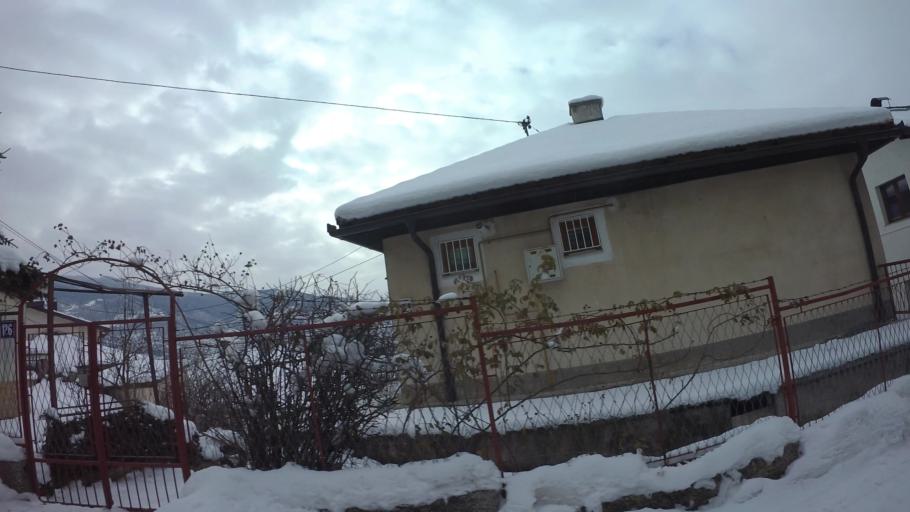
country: BA
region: Federation of Bosnia and Herzegovina
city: Kobilja Glava
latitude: 43.8678
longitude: 18.4349
